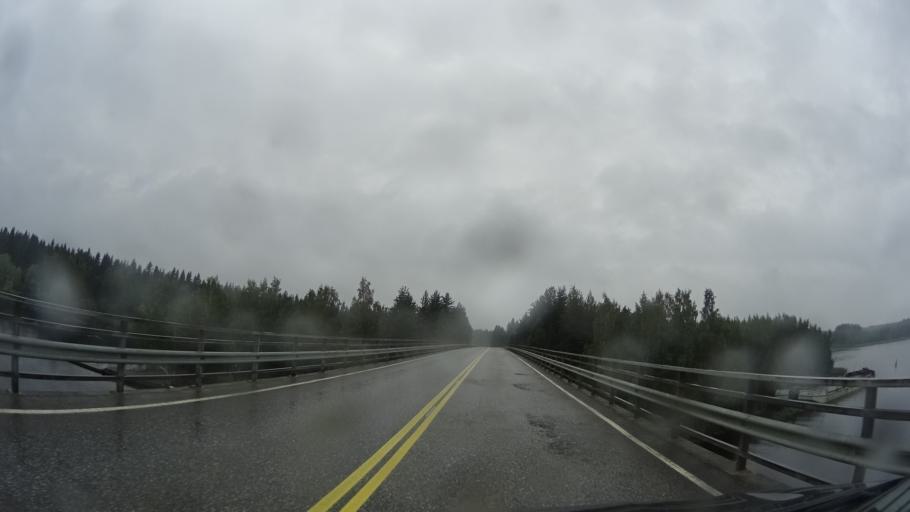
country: FI
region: North Karelia
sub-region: Keski-Karjala
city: Raeaekkylae
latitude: 62.3146
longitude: 29.5142
